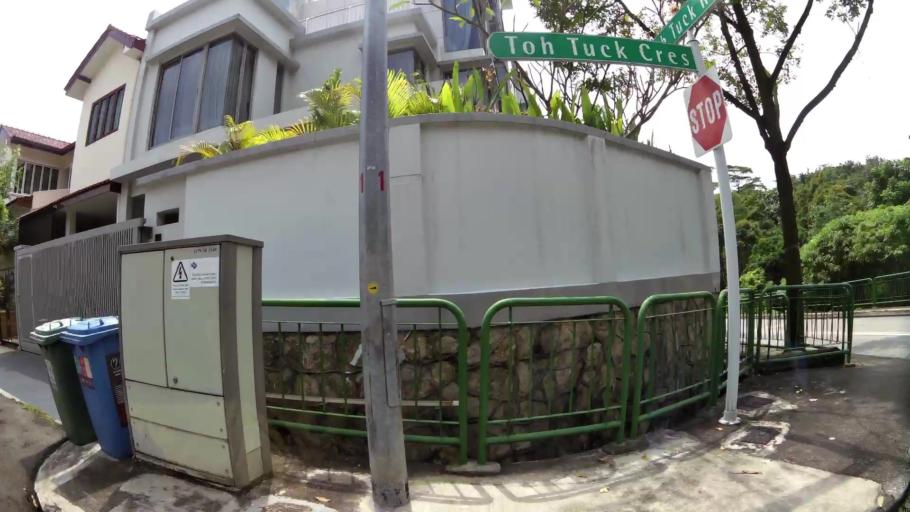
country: SG
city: Singapore
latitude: 1.3377
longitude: 103.7644
